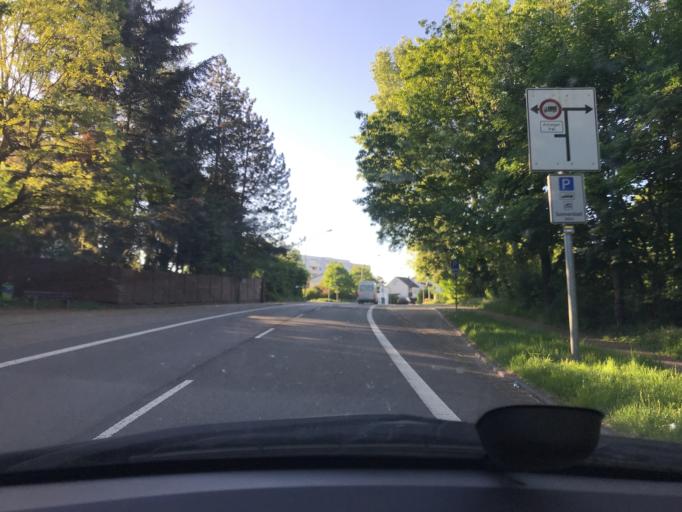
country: DE
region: Saarland
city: Saarlouis
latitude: 49.3379
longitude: 6.7685
